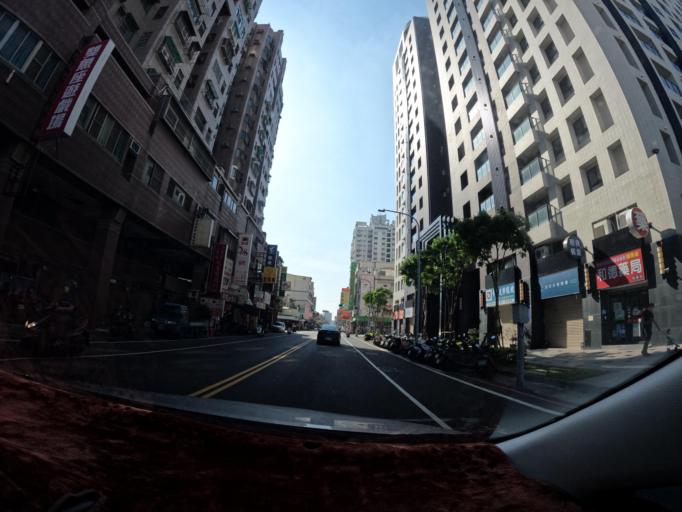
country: TW
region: Taiwan
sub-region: Tainan
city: Tainan
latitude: 23.0117
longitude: 120.2465
